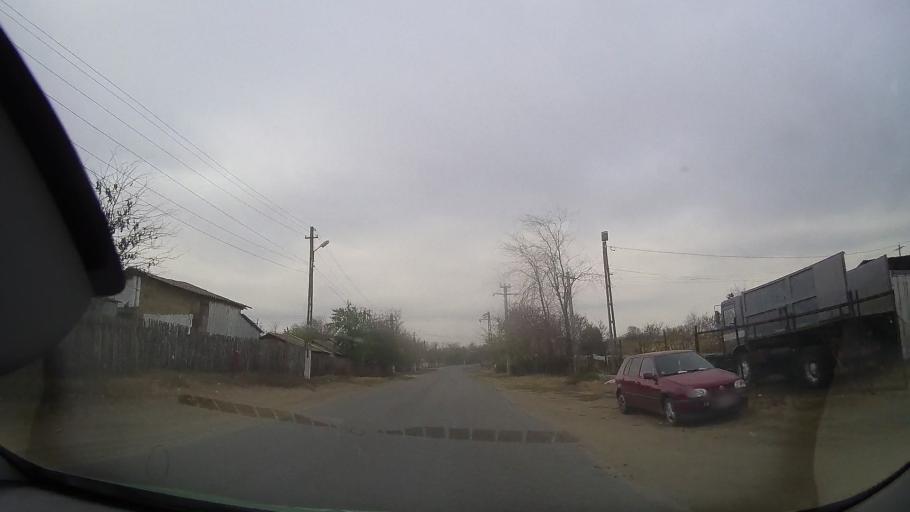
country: RO
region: Buzau
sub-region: Comuna Largu
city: Largu
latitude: 44.9743
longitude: 27.1523
